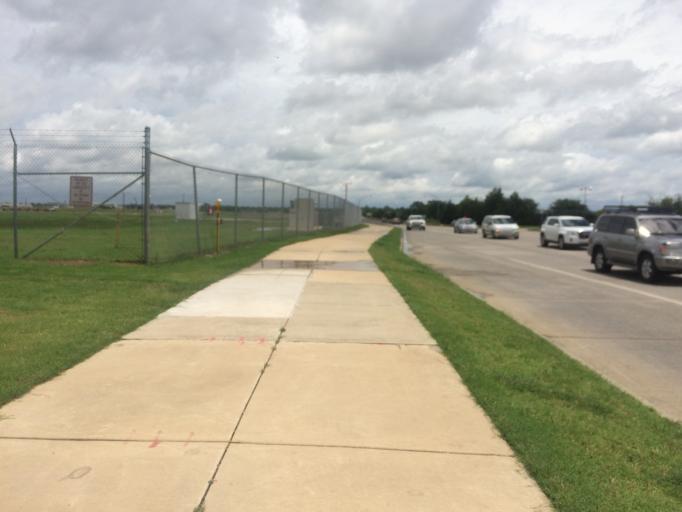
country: US
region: Oklahoma
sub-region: Cleveland County
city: Norman
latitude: 35.2331
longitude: -97.4796
